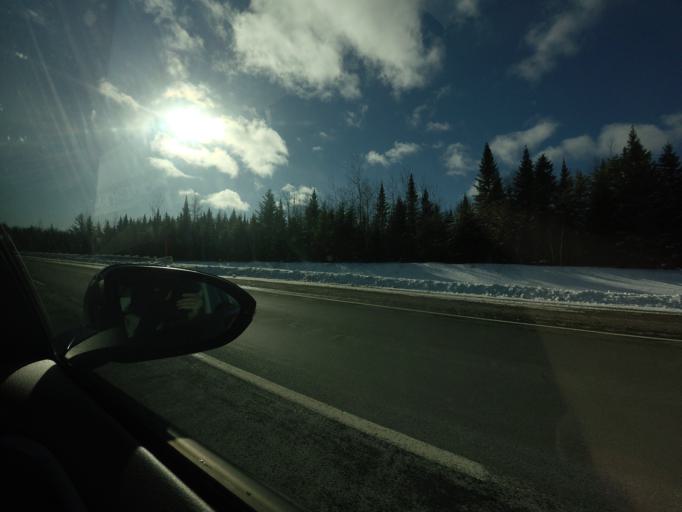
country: CA
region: New Brunswick
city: Fredericton
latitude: 45.8780
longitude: -66.6341
